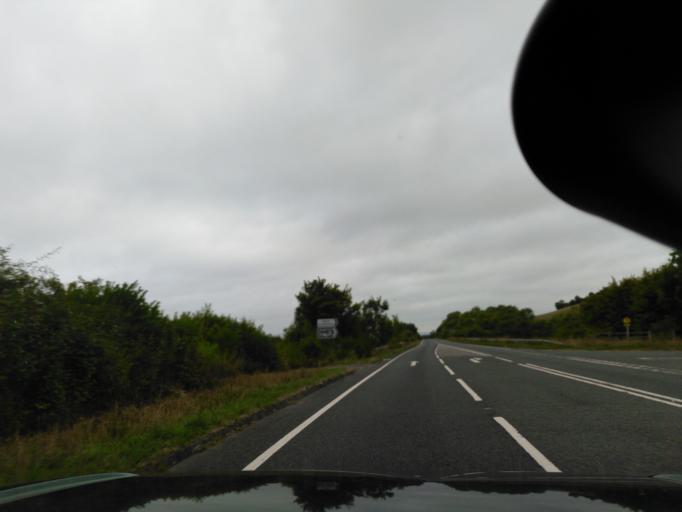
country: GB
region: England
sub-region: Wiltshire
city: Upton Scudamore
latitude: 51.2327
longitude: -2.1882
